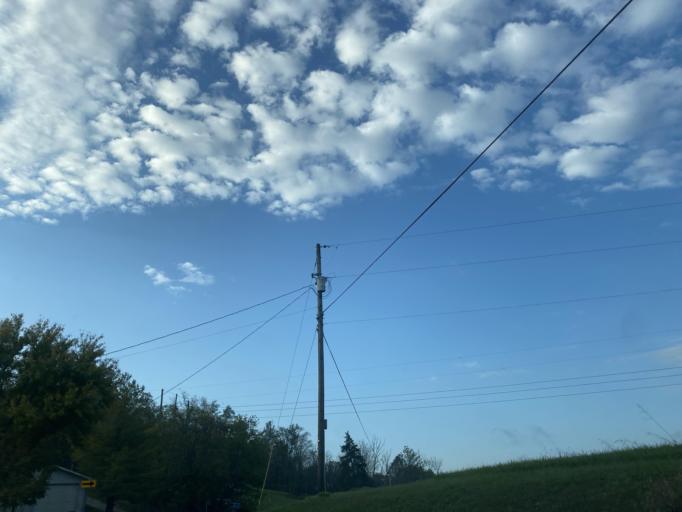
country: US
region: Kentucky
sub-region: Pendleton County
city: Falmouth
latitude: 38.7651
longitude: -84.3386
